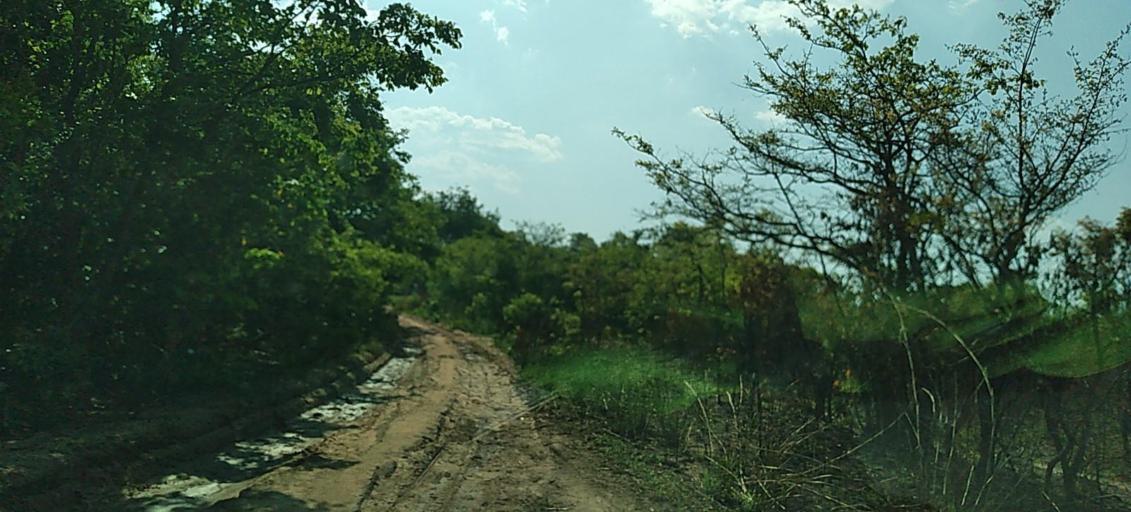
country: ZM
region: North-Western
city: Mwinilunga
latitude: -11.2975
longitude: 24.8603
